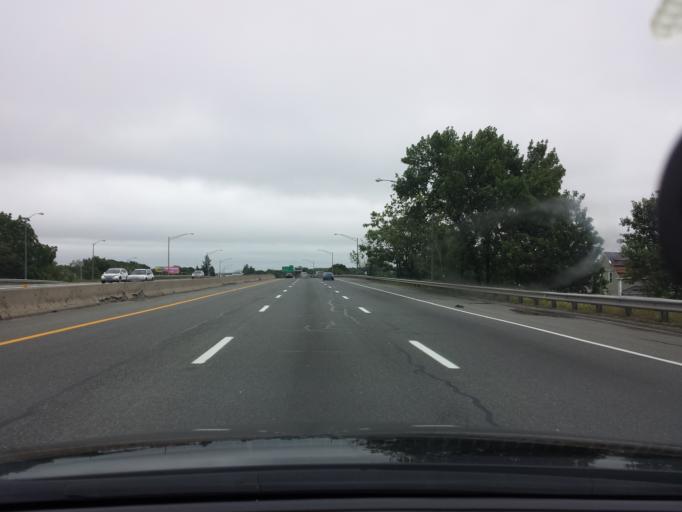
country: US
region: Rhode Island
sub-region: Providence County
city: East Providence
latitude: 41.8156
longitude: -71.3734
